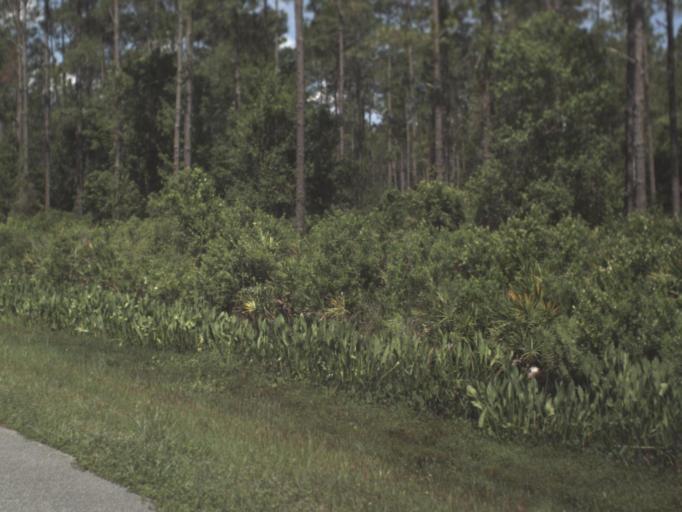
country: US
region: Florida
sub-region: Levy County
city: Bronson
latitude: 29.3386
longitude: -82.7493
